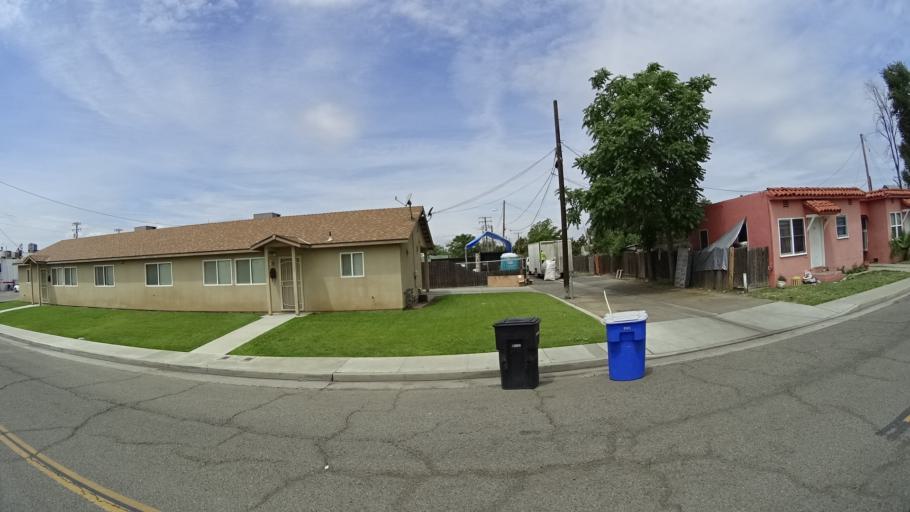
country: US
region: California
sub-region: Kings County
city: Hanford
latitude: 36.3284
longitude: -119.6396
